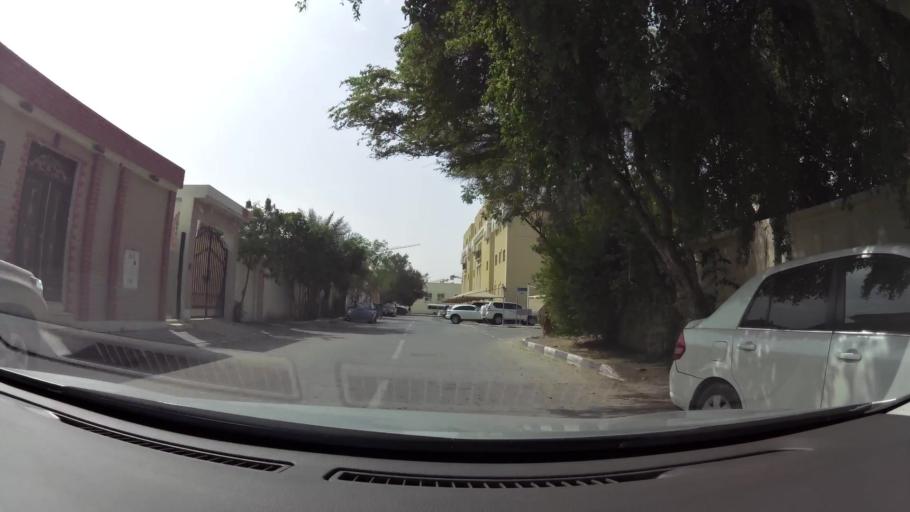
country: QA
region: Baladiyat ar Rayyan
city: Ar Rayyan
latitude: 25.3061
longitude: 51.4753
